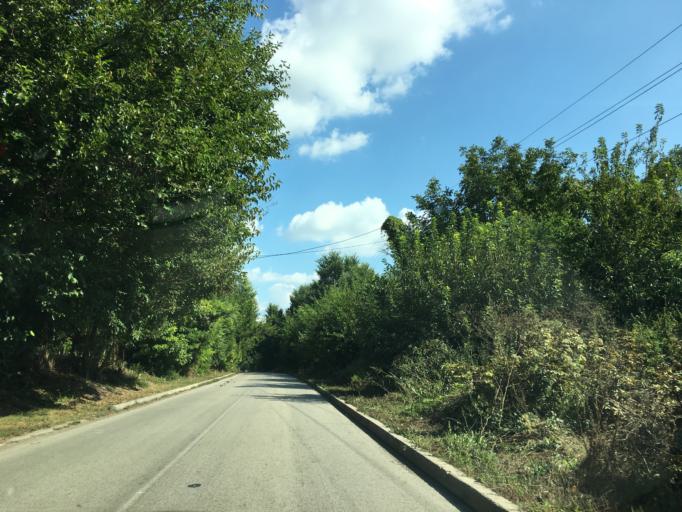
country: BG
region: Montana
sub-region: Obshtina Lom
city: Lom
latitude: 43.8228
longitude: 23.2039
